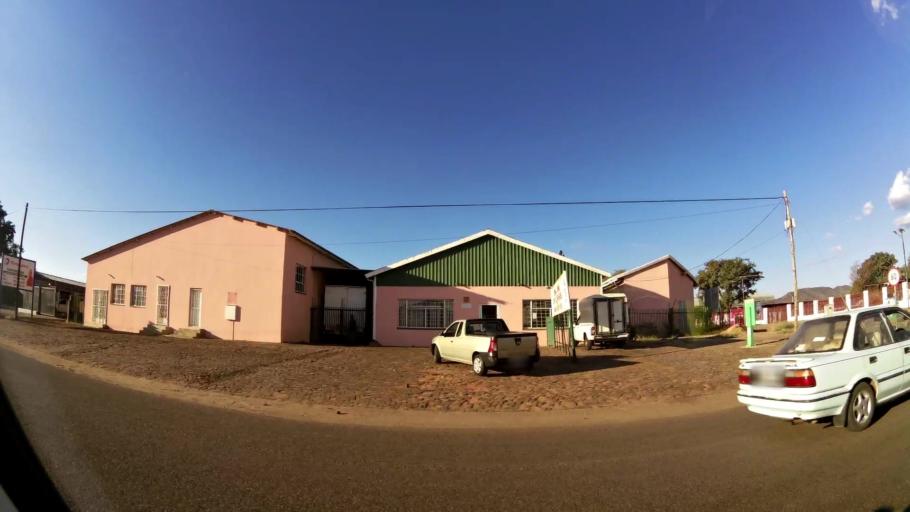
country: ZA
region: Limpopo
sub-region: Waterberg District Municipality
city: Mokopane
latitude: -24.1729
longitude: 29.0004
